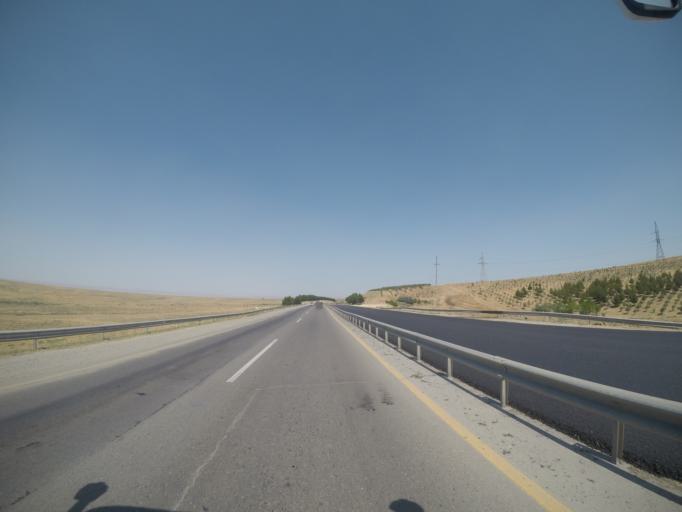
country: AZ
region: Haciqabul
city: Haciqabul
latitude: 40.0466
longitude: 48.9816
